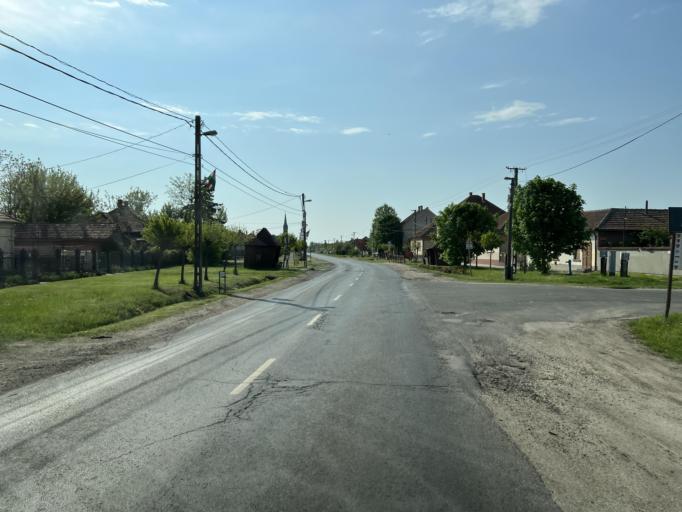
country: HU
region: Pest
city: Jaszkarajeno
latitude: 47.0586
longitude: 20.0603
